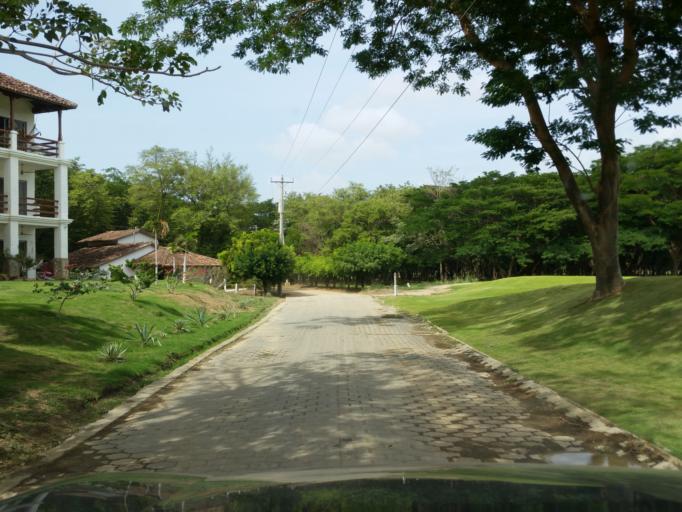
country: NI
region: Rivas
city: Tola
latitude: 11.4135
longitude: -86.0520
